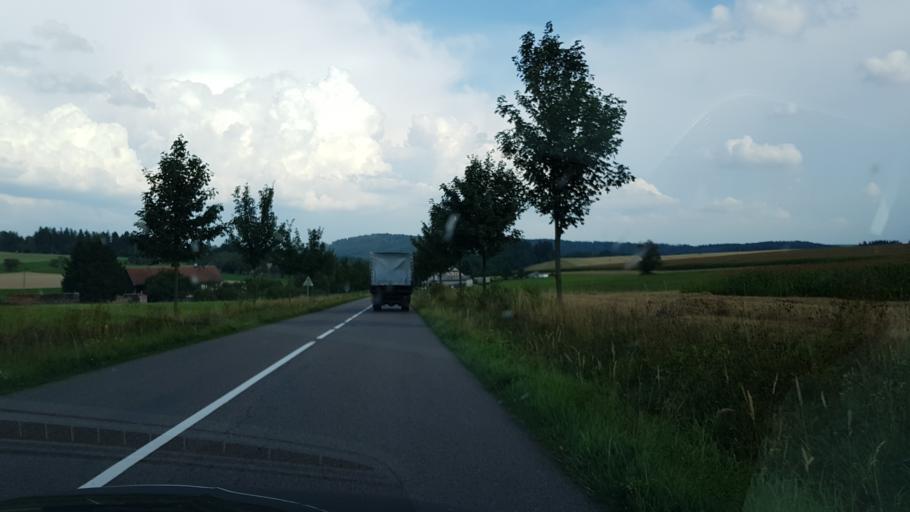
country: CZ
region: Pardubicky
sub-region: Okres Usti nad Orlici
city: Kunvald
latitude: 50.0910
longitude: 16.5428
